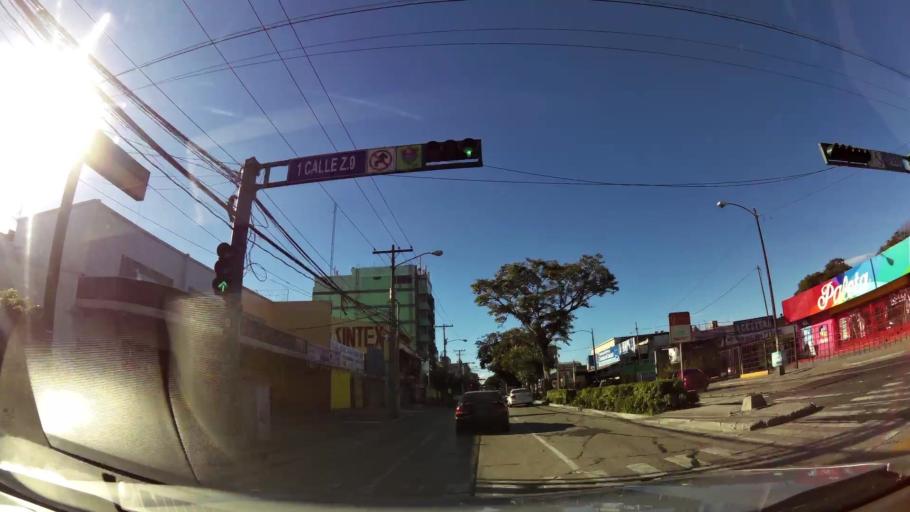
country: GT
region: Guatemala
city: Guatemala City
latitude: 14.6142
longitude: -90.5178
